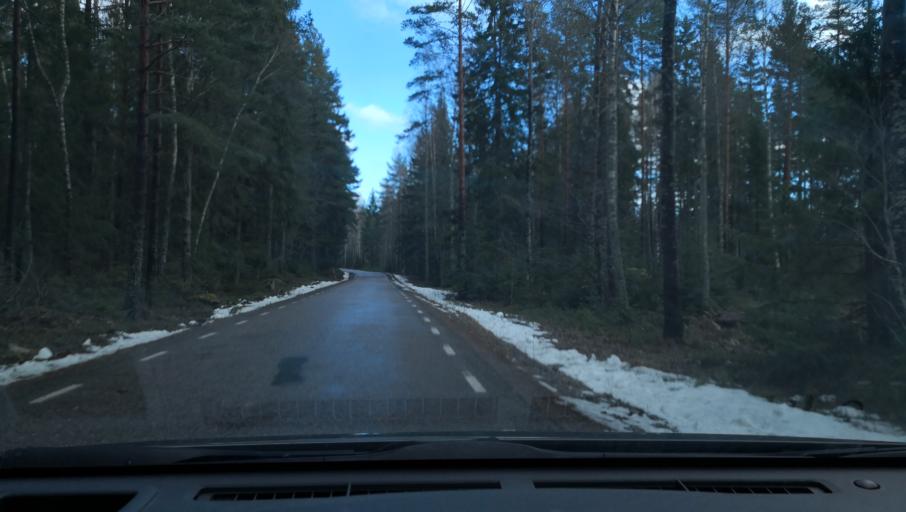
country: SE
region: Vaestmanland
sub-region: Arboga Kommun
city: Arboga
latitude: 59.3350
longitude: 15.7197
